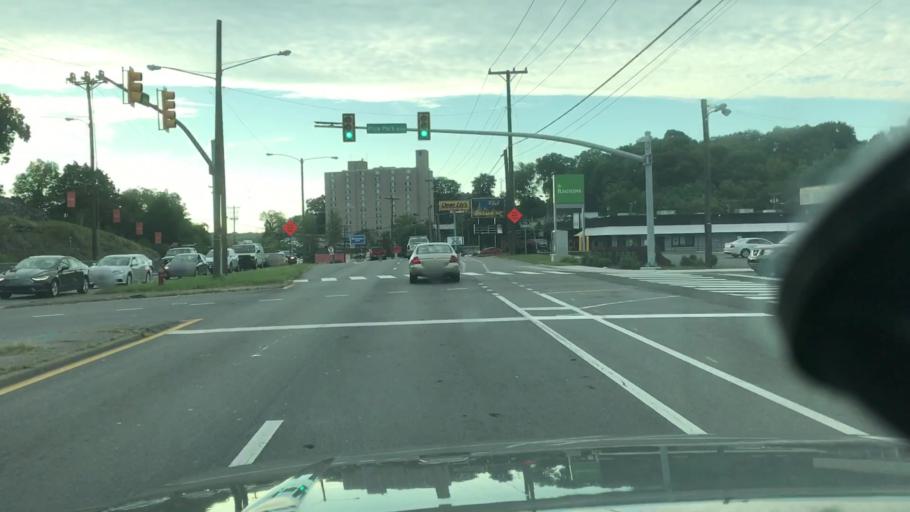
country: US
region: Tennessee
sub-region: Davidson County
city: Nashville
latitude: 36.1341
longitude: -86.7228
